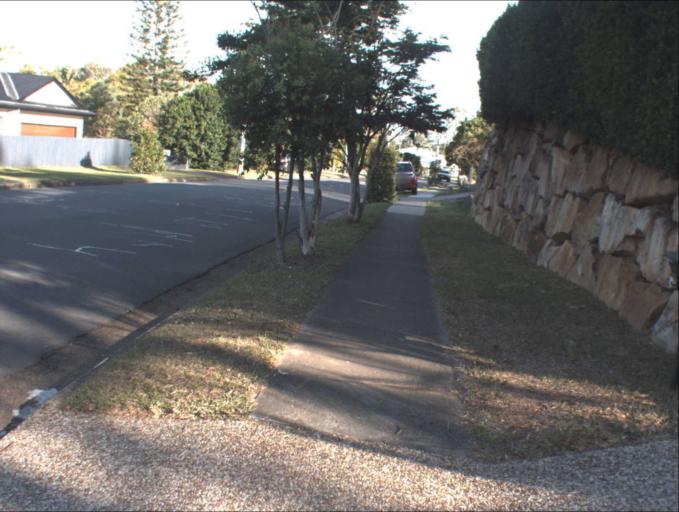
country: AU
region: Queensland
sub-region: Logan
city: Beenleigh
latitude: -27.6731
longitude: 153.2040
